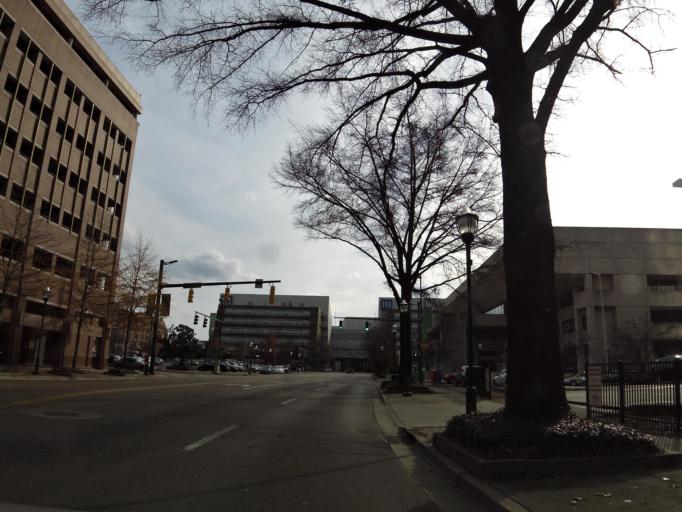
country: US
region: Tennessee
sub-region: Hamilton County
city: Chattanooga
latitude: 35.0454
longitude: -85.3105
